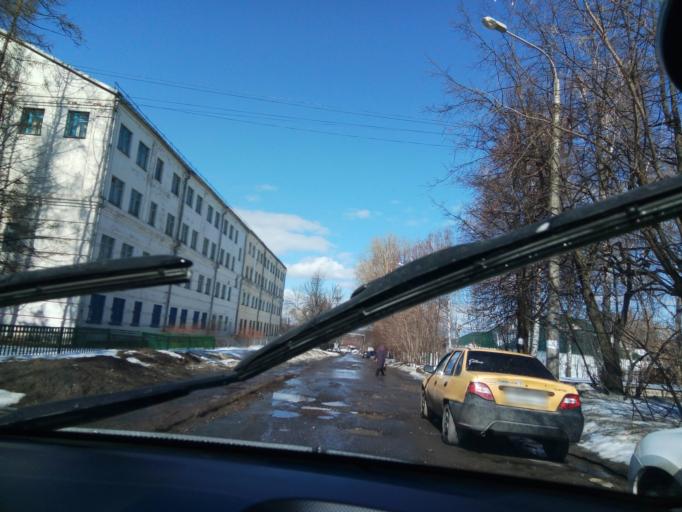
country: RU
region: Chuvashia
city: Novyye Lapsary
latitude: 56.1086
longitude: 47.1730
